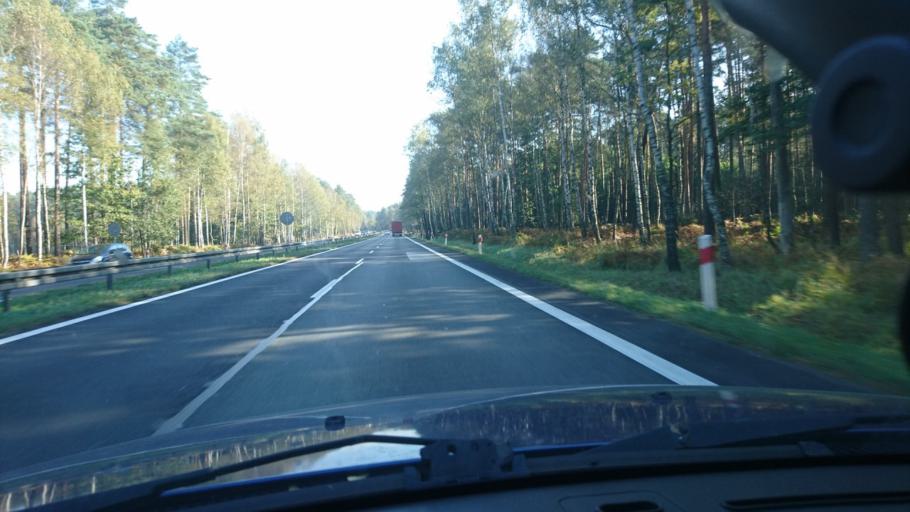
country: PL
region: Silesian Voivodeship
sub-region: Tychy
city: Cielmice
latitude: 50.0725
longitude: 18.9916
